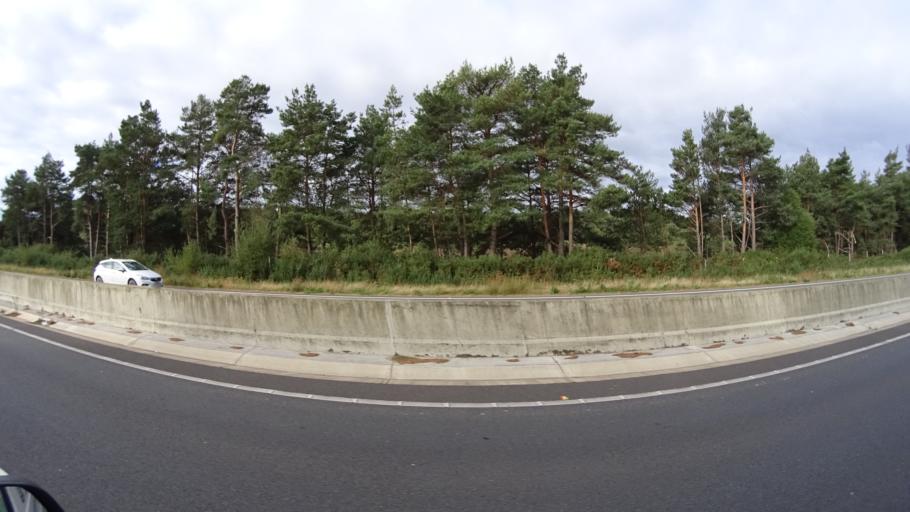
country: GB
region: England
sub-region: Dorset
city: Christchurch
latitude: 50.7741
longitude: -1.8072
